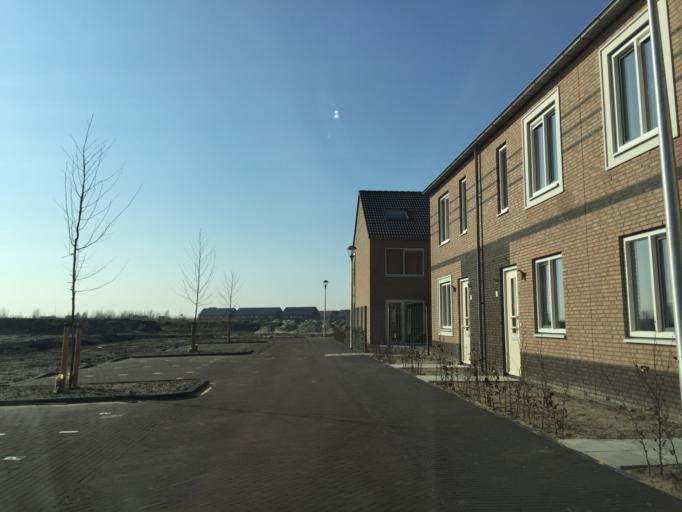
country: NL
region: South Holland
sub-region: Gemeente Pijnacker-Nootdorp
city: Pijnacker
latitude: 52.0015
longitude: 4.4460
